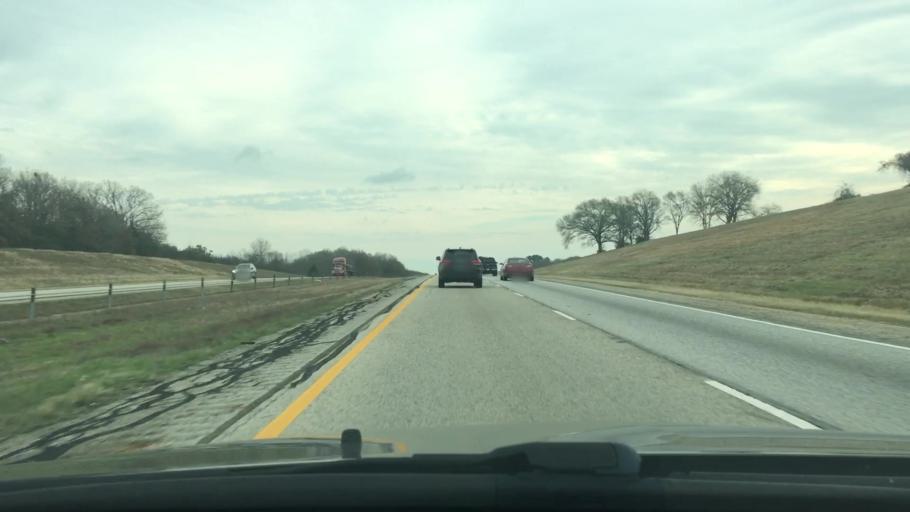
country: US
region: Texas
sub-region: Leon County
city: Centerville
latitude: 31.2885
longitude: -95.9952
